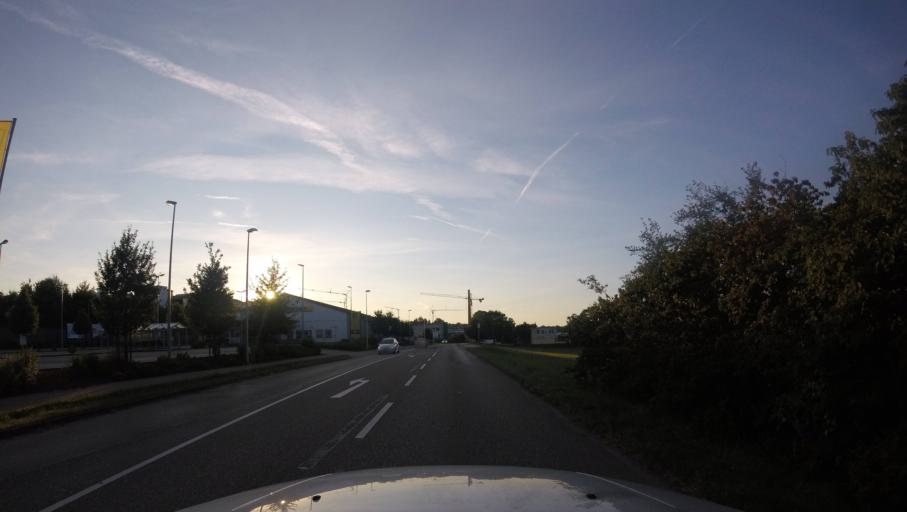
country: DE
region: Baden-Wuerttemberg
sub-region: Regierungsbezirk Stuttgart
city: Allmersbach im Tal
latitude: 48.9239
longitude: 9.4832
